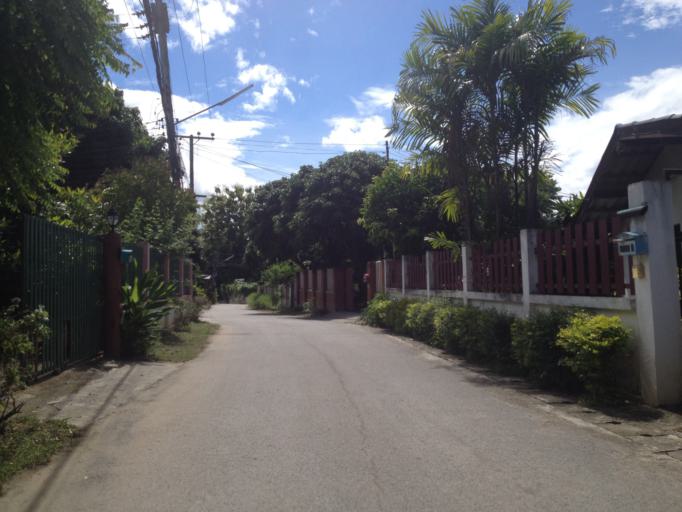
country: TH
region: Chiang Mai
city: Hang Dong
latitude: 18.7248
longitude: 98.9126
